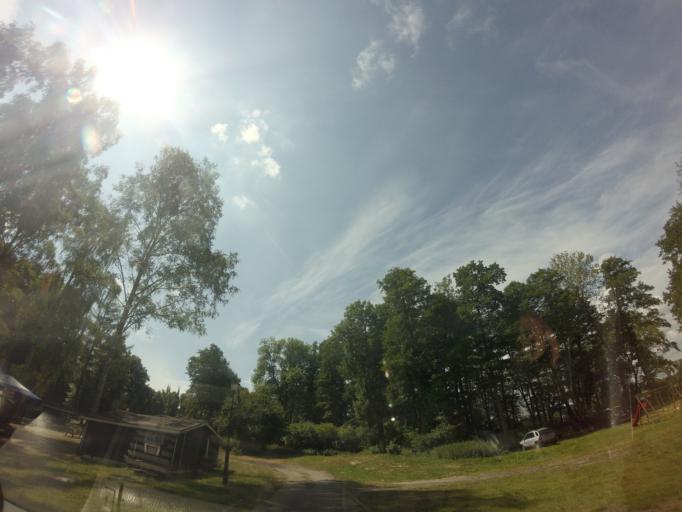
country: PL
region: West Pomeranian Voivodeship
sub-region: Powiat choszczenski
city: Drawno
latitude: 53.2159
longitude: 15.7618
